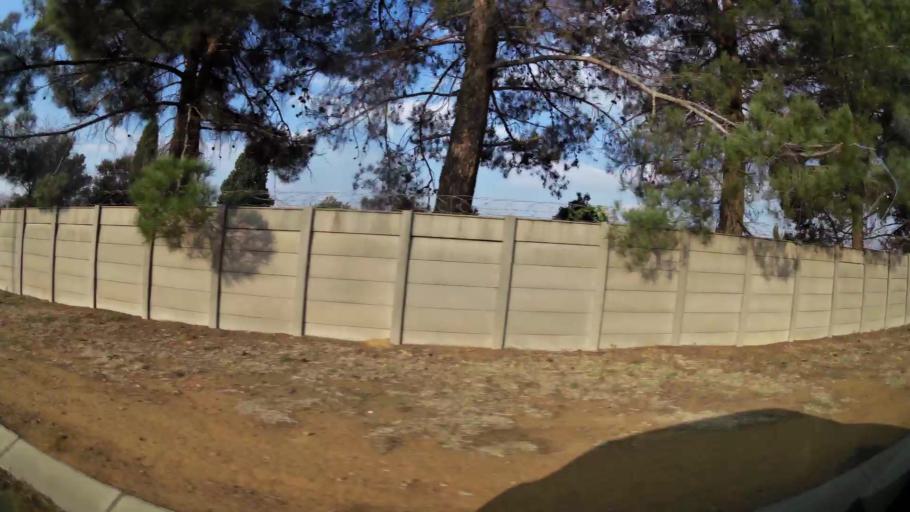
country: ZA
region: Gauteng
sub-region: Ekurhuleni Metropolitan Municipality
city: Benoni
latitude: -26.1087
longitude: 28.2809
